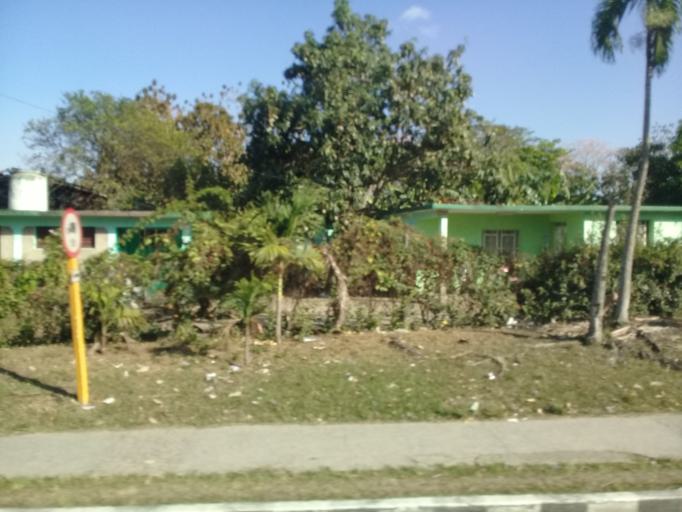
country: CU
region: Pinar del Rio
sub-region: Municipio de Pinar del Rio
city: Pinar del Rio
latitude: 22.4290
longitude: -83.6880
